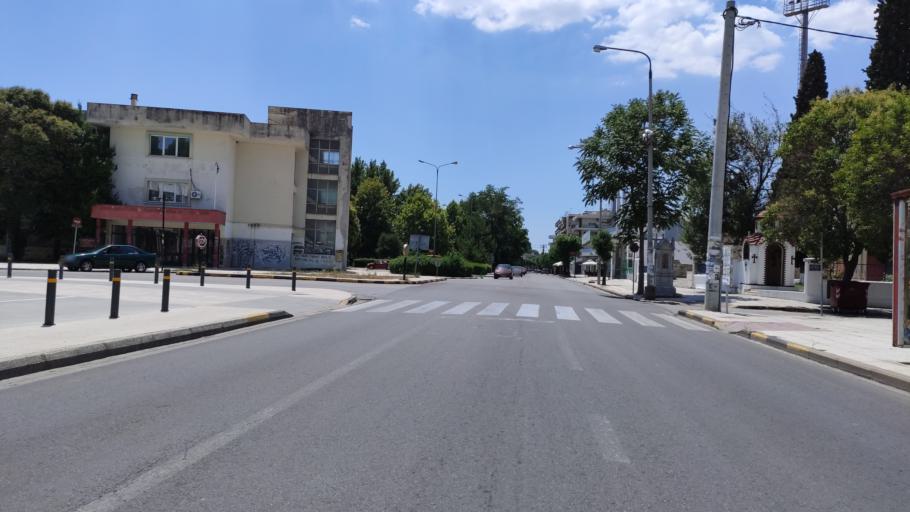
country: GR
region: East Macedonia and Thrace
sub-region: Nomos Rodopis
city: Komotini
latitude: 41.1151
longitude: 25.3980
